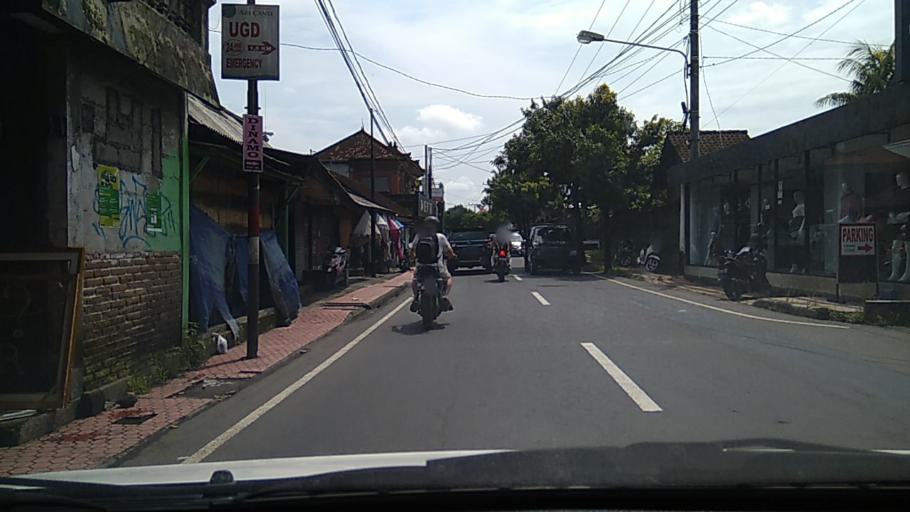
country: ID
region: Bali
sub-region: Kabupaten Gianyar
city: Ubud
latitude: -8.5239
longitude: 115.2705
